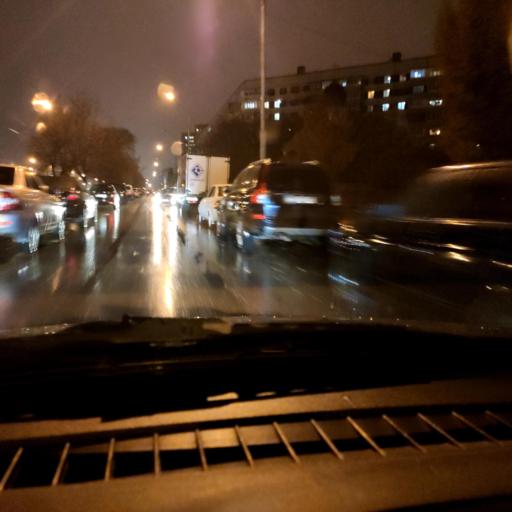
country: RU
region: Samara
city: Tol'yatti
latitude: 53.5282
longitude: 49.3337
